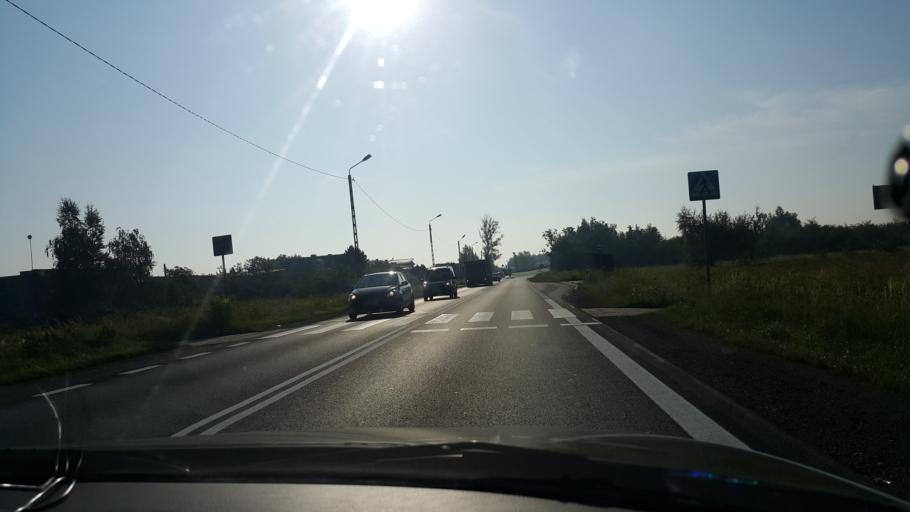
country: PL
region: Masovian Voivodeship
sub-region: Radom
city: Radom
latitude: 51.4134
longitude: 21.2305
